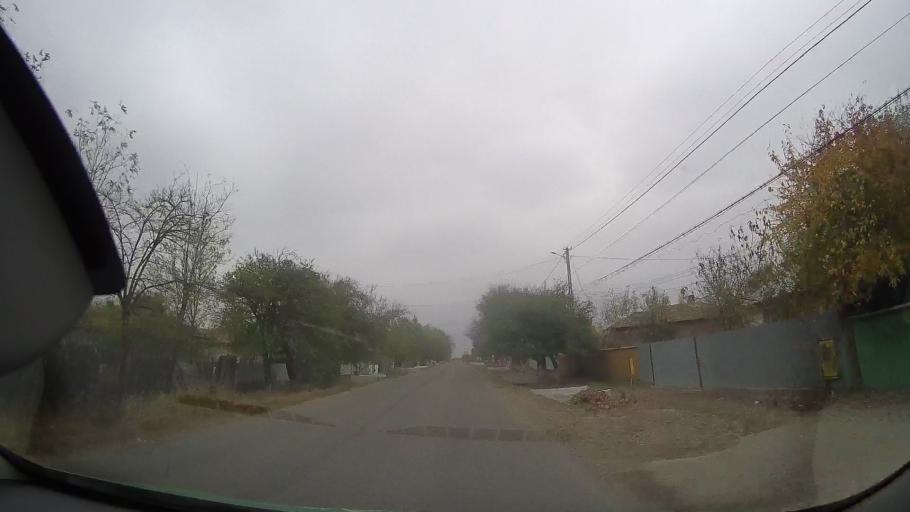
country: RO
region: Buzau
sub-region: Comuna Glodeanu-Silistea
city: Glodeanu-Silistea
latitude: 44.8189
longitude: 26.8384
